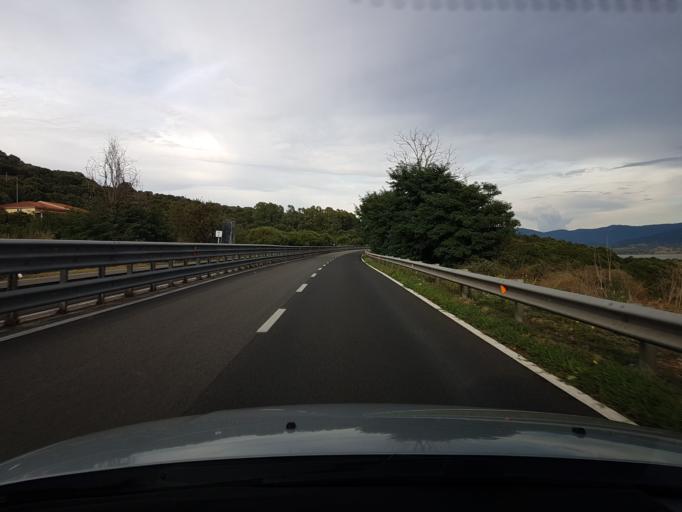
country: IT
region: Sardinia
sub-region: Provincia di Oristano
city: Soddi
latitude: 40.1485
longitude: 8.8869
